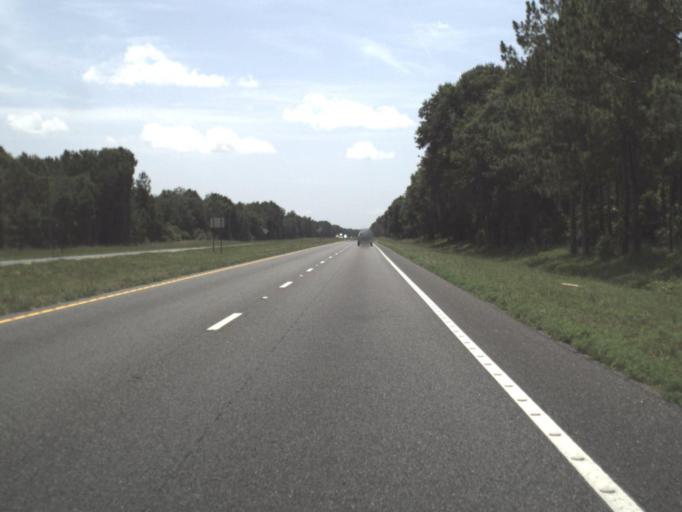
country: US
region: Florida
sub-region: Taylor County
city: Perry
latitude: 30.0092
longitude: -83.5172
